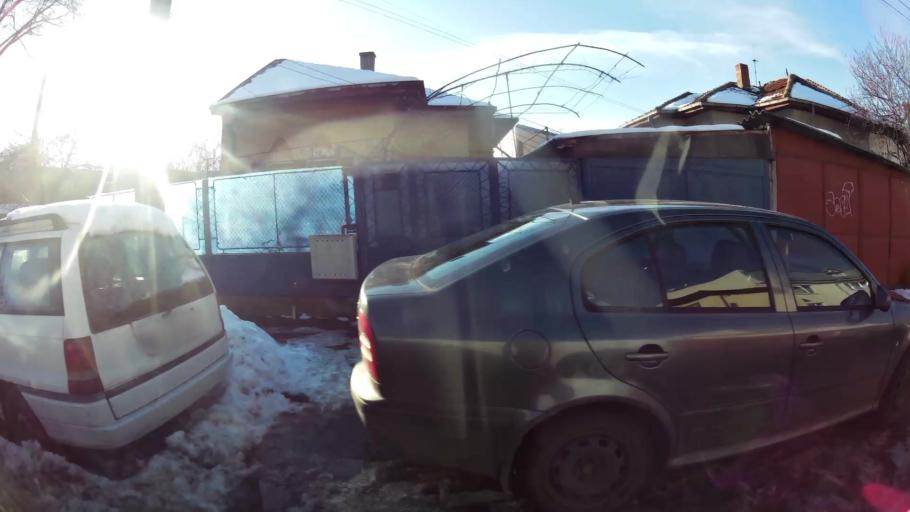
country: RO
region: Bucuresti
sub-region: Municipiul Bucuresti
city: Bucuresti
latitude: 44.3973
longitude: 26.0913
